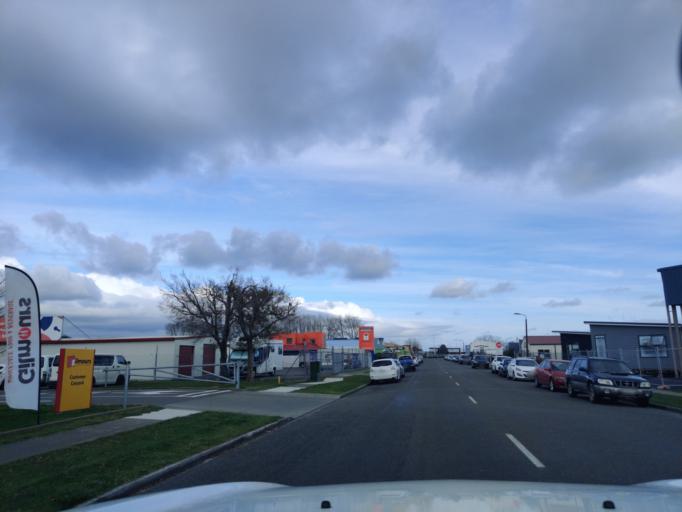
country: NZ
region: Manawatu-Wanganui
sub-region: Palmerston North City
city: Palmerston North
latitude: -40.3389
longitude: 175.6006
